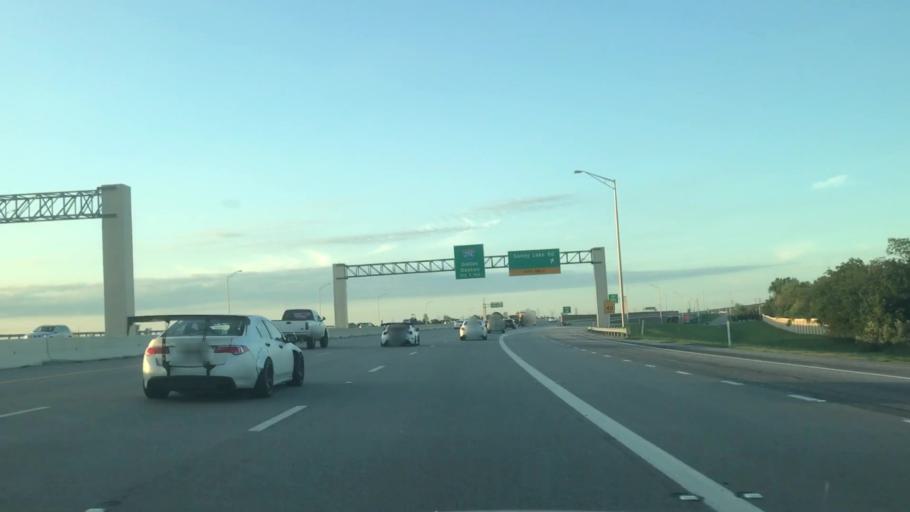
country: US
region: Texas
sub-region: Dallas County
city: Carrollton
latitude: 32.9634
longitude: -96.9321
